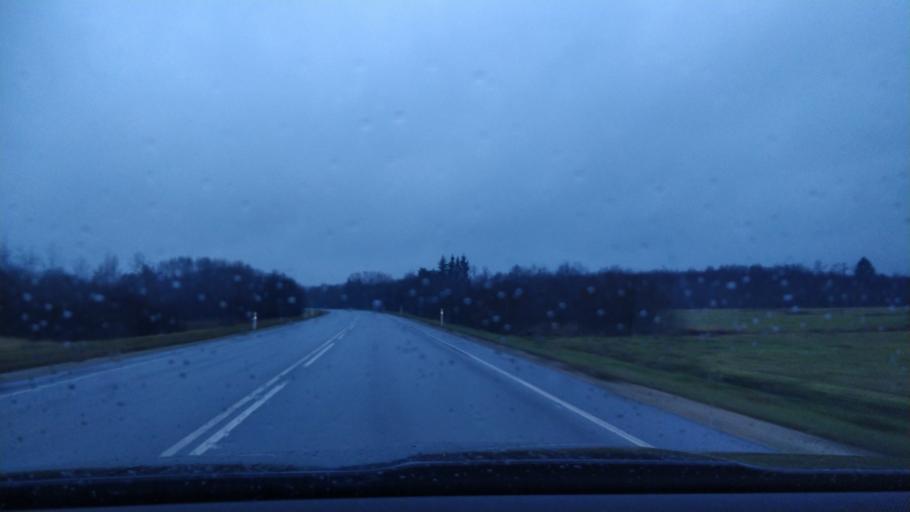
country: EE
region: Laeaene
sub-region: Lihula vald
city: Lihula
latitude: 58.8340
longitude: 24.0550
